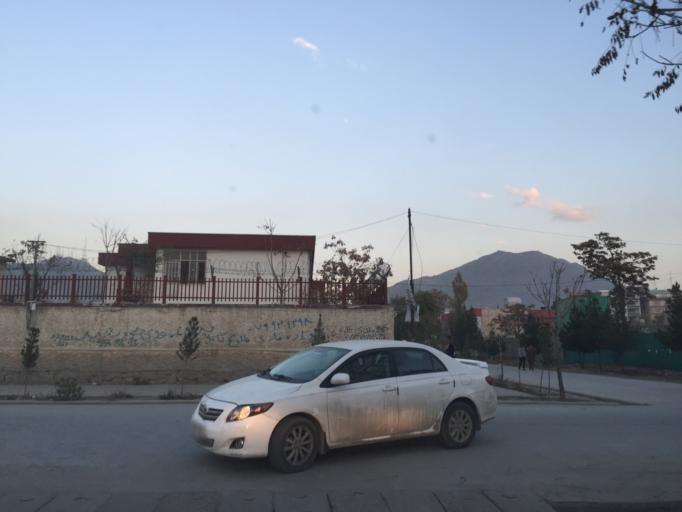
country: AF
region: Kabul
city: Kabul
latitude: 34.5075
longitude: 69.1403
